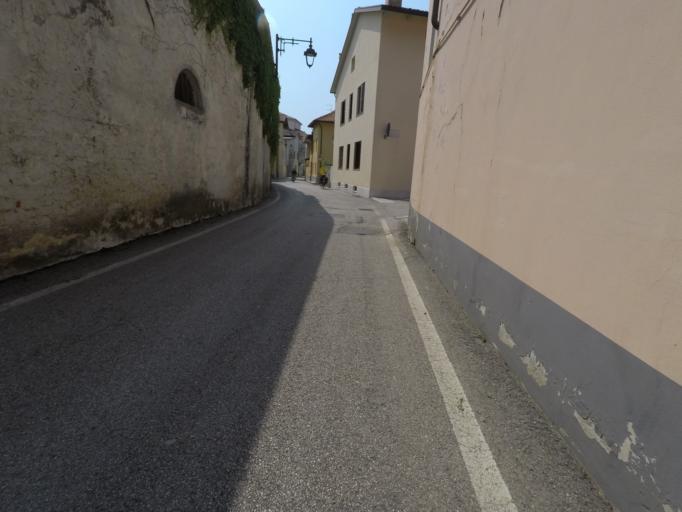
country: IT
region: Friuli Venezia Giulia
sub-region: Provincia di Pordenone
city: Montereale Valcellina
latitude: 46.1622
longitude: 12.6610
